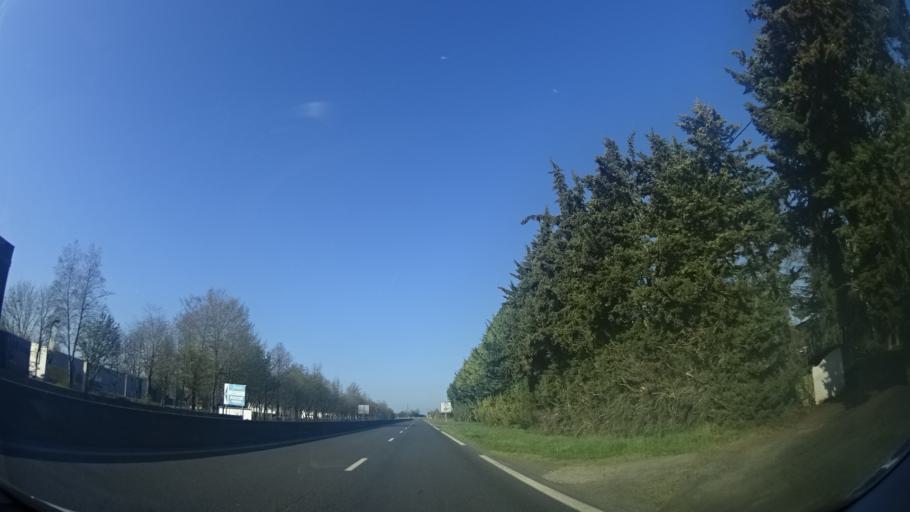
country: FR
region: Pays de la Loire
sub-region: Departement de Maine-et-Loire
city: Distre
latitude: 47.2329
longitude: -0.1193
